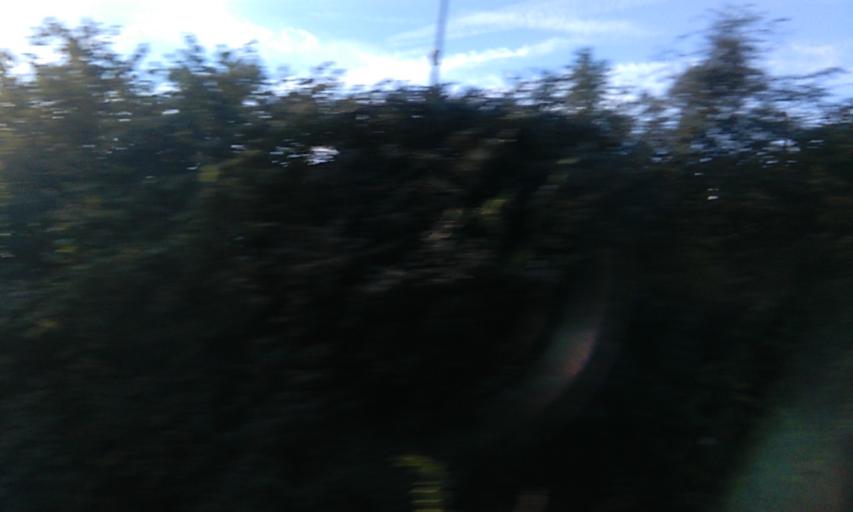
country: GB
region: England
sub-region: Leicestershire
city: Loughborough
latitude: 52.7777
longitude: -1.1932
